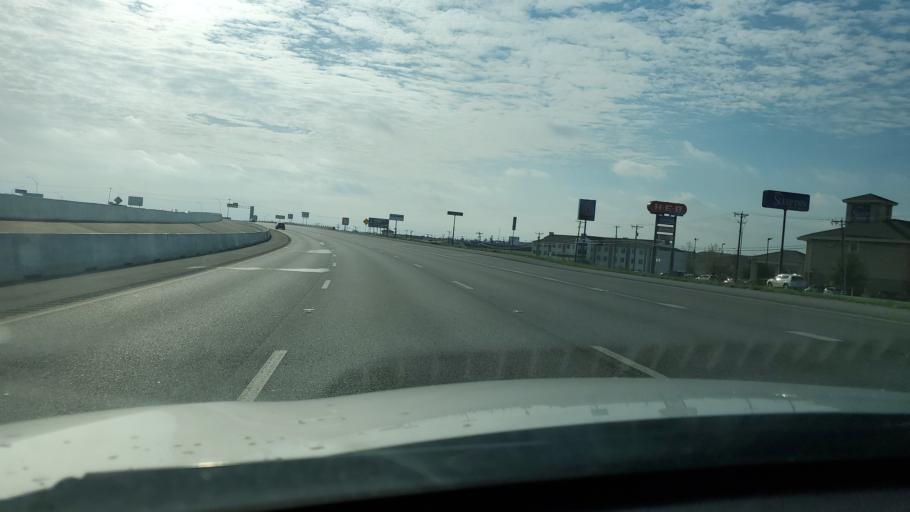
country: US
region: Texas
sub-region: Bell County
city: Killeen
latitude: 31.0962
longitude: -97.7368
